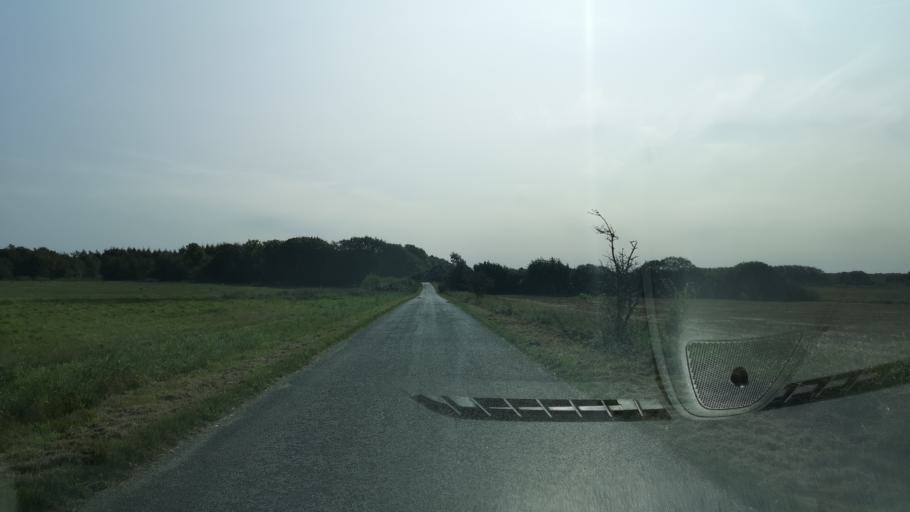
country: DK
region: Central Jutland
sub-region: Herning Kommune
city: Herning
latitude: 56.1729
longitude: 8.9544
